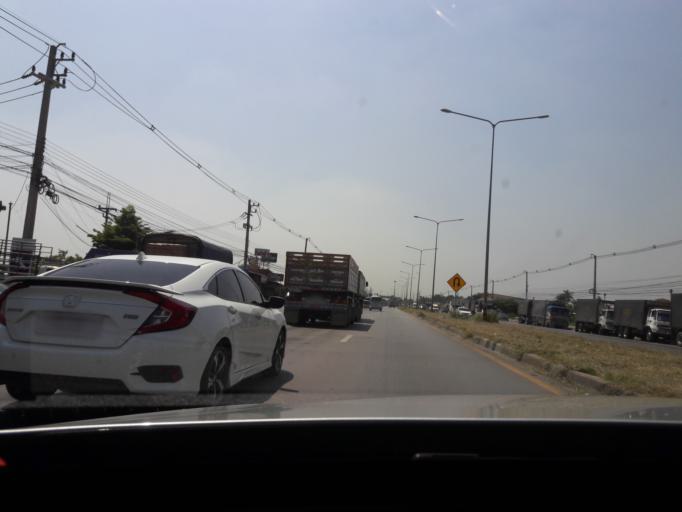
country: TH
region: Samut Sakhon
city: Krathum Baen
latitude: 13.6541
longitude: 100.3064
